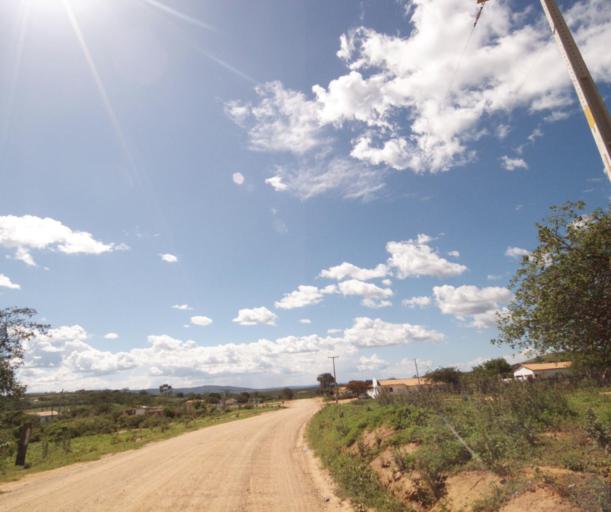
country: BR
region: Bahia
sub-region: Pocoes
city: Pocoes
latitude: -14.2550
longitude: -40.7305
